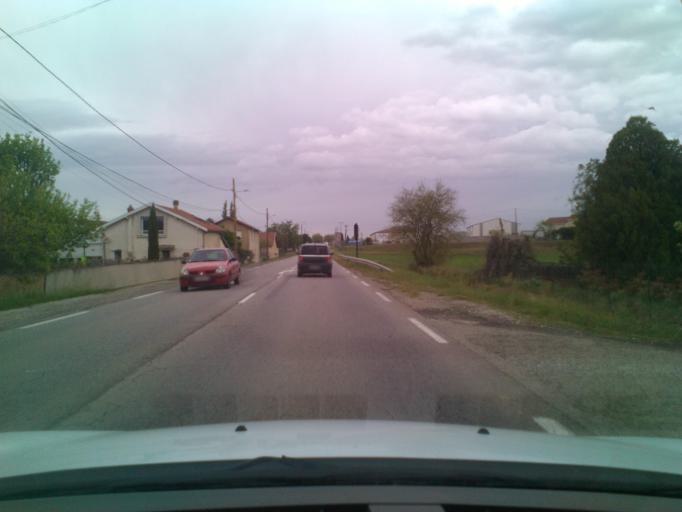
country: FR
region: Rhone-Alpes
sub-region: Departement de la Drome
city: Beausemblant
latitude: 45.2236
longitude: 4.8168
